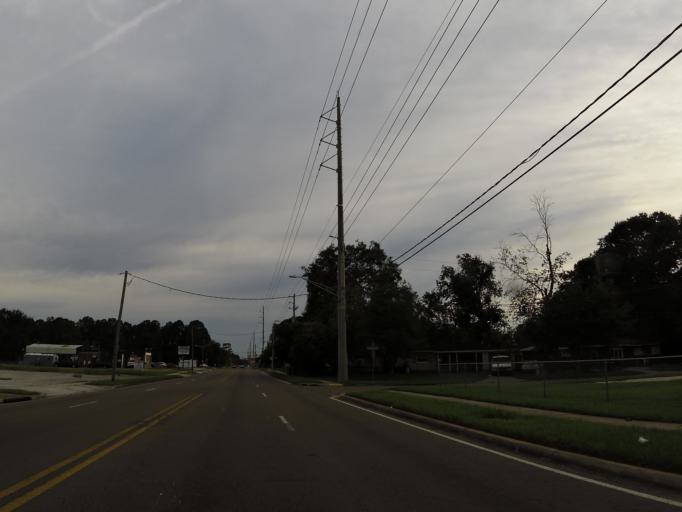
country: US
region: Florida
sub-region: Duval County
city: Jacksonville
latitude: 30.4006
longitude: -81.7233
